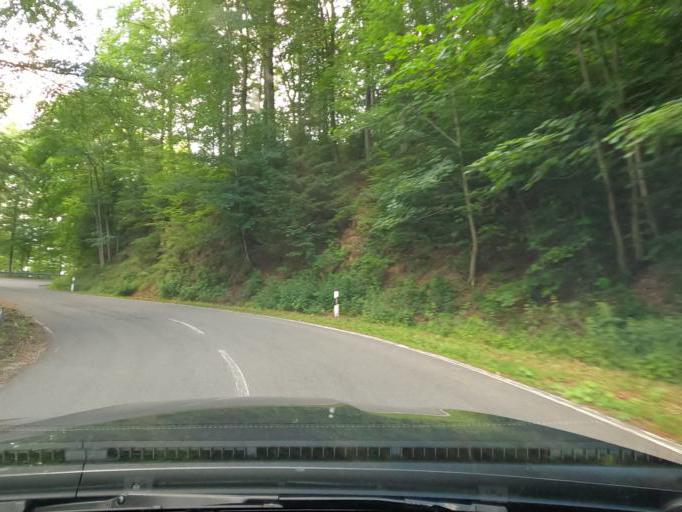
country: DE
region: Lower Saxony
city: Clausthal-Zellerfeld
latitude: 51.7641
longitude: 10.3099
